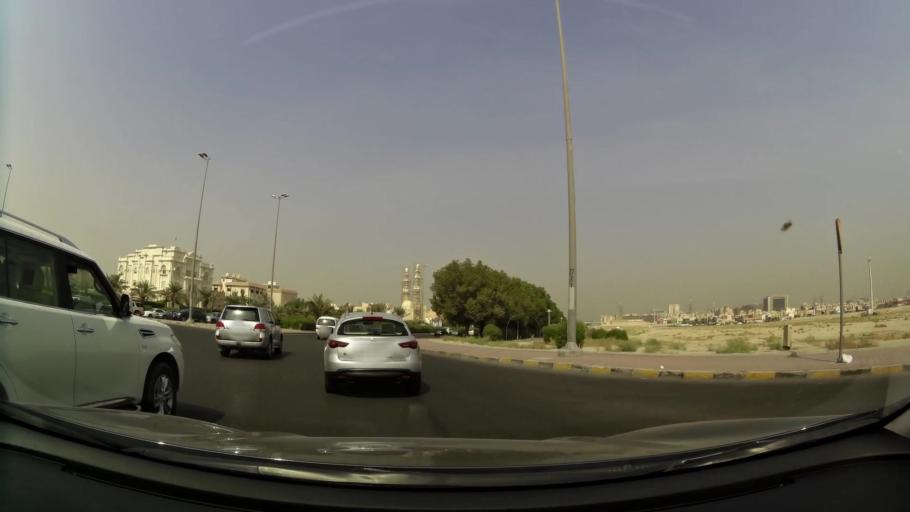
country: KW
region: Al Asimah
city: Ar Rabiyah
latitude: 29.2889
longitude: 47.9065
